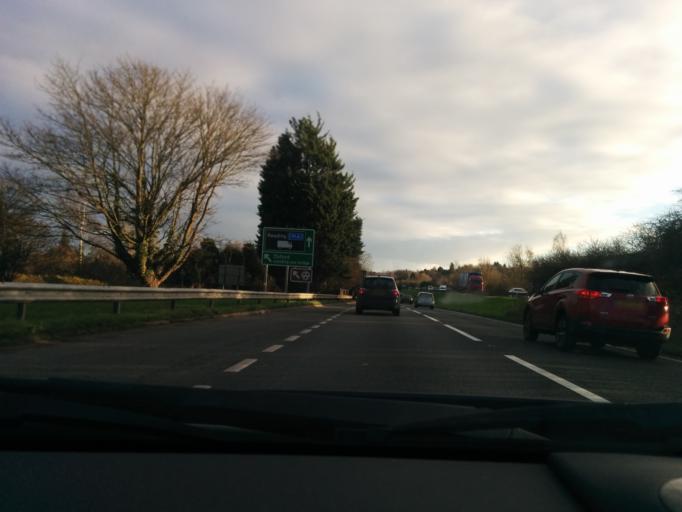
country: GB
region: England
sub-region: Oxfordshire
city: Oxford
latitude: 51.7343
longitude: -1.2680
